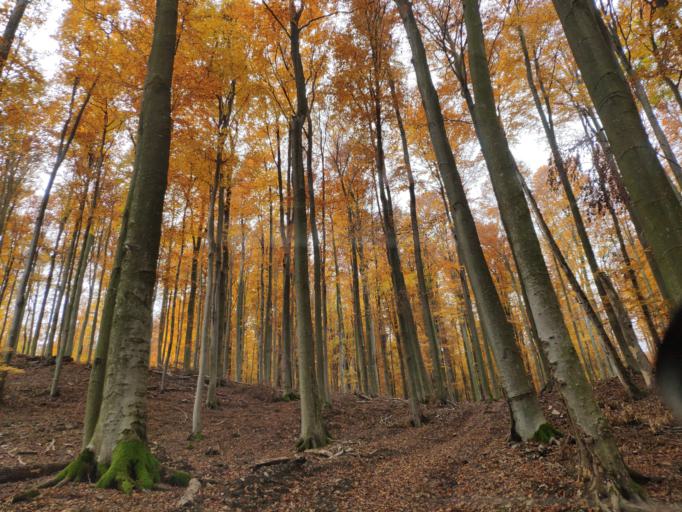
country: SK
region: Kosicky
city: Moldava nad Bodvou
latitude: 48.7350
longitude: 21.0151
